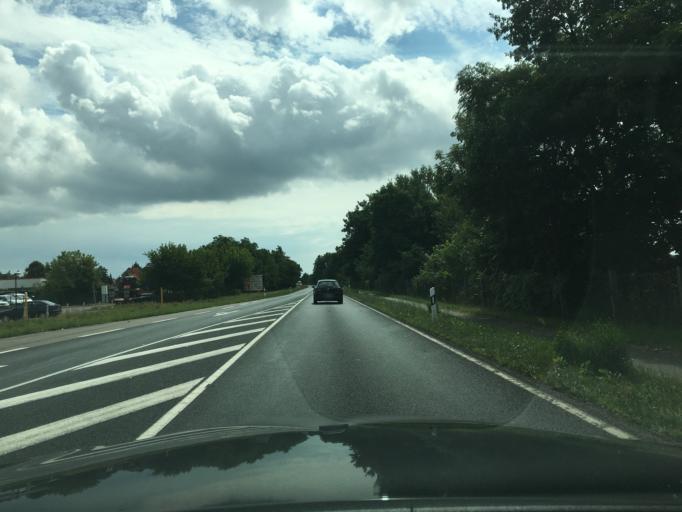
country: DE
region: Saxony-Anhalt
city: Wolfen
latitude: 51.6497
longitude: 12.2744
